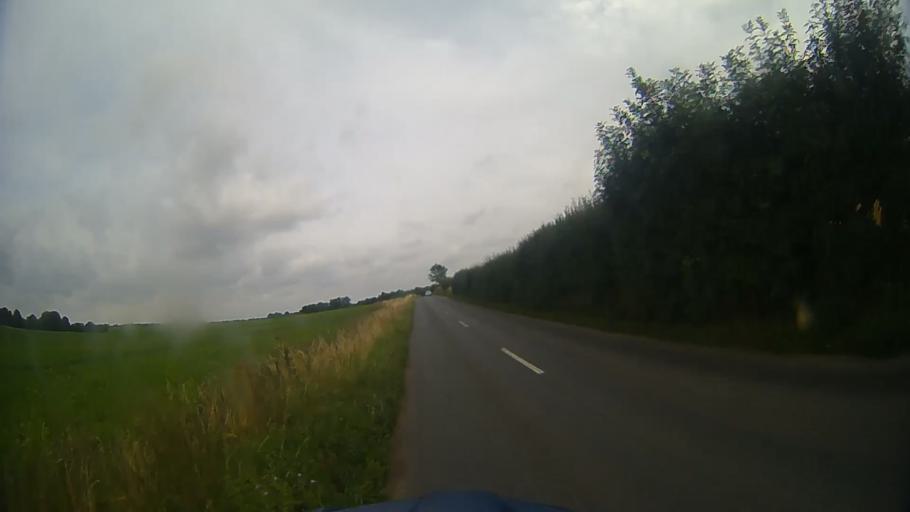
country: GB
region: England
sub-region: Hampshire
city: Basingstoke
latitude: 51.2539
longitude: -1.1611
